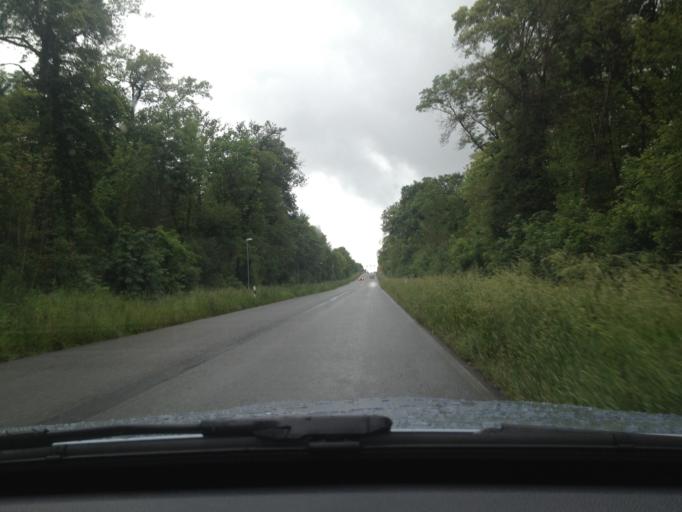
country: DE
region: Baden-Wuerttemberg
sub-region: Karlsruhe Region
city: Ketsch
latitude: 49.3767
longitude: 8.5530
